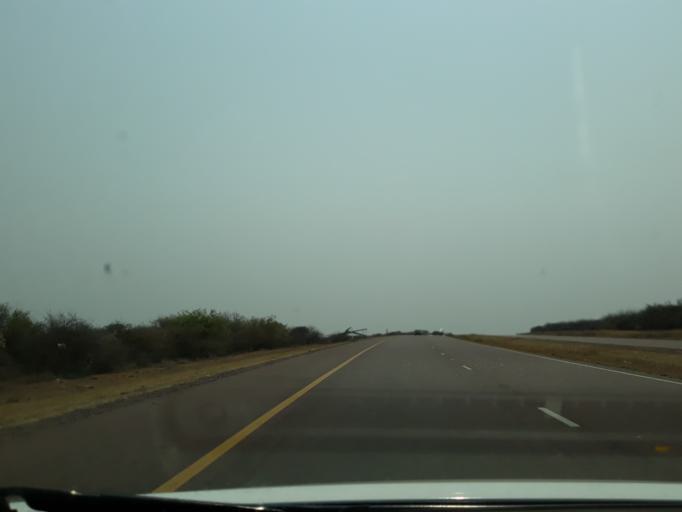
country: BW
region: Kgatleng
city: Bokaa
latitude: -24.4187
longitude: 26.0479
